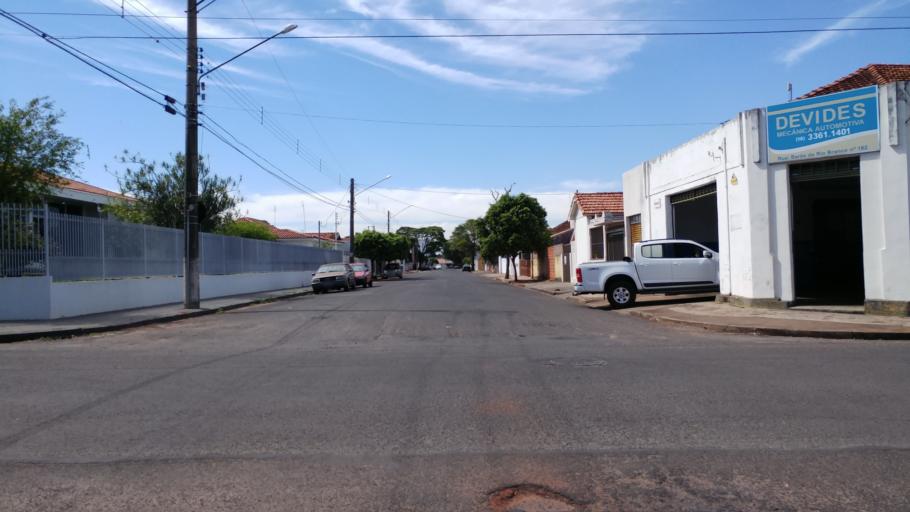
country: BR
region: Sao Paulo
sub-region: Paraguacu Paulista
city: Paraguacu Paulista
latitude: -22.4116
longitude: -50.5746
